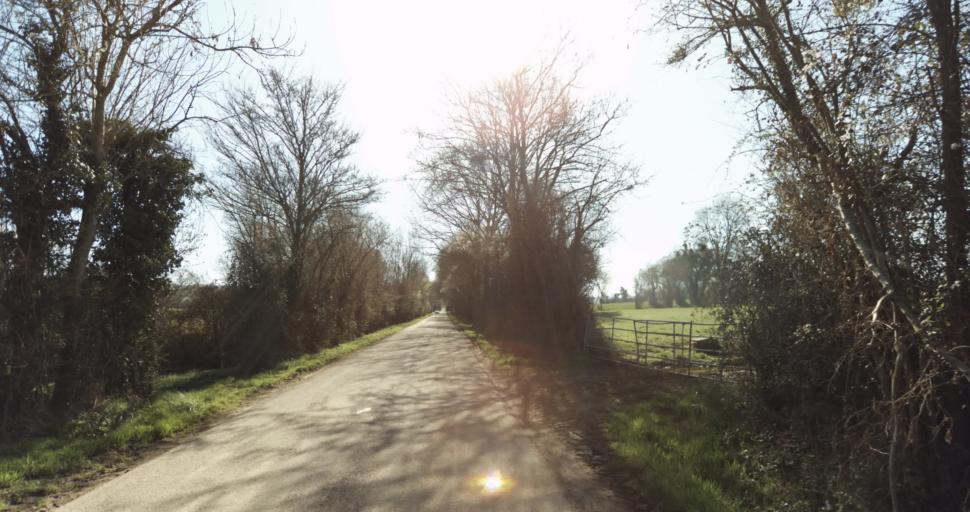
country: FR
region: Lower Normandy
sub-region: Departement du Calvados
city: Saint-Pierre-sur-Dives
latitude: 48.9702
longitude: 0.0490
